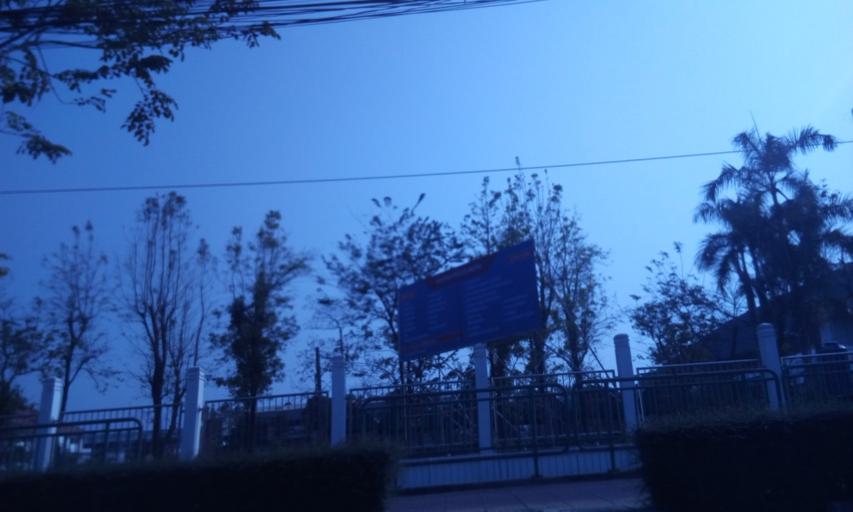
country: TH
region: Bangkok
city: Don Mueang
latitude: 13.9292
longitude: 100.5792
